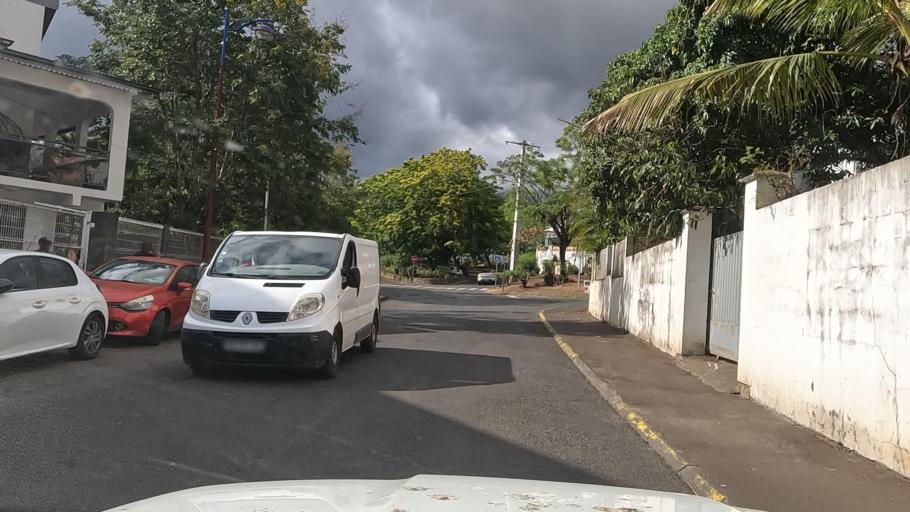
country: RE
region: Reunion
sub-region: Reunion
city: Saint-Louis
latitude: -21.2739
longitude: 55.4039
